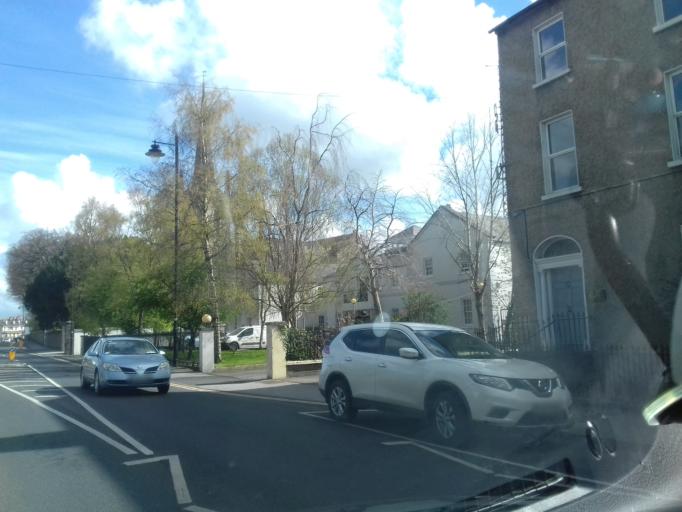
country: IE
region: Ulster
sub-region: An Cabhan
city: Cavan
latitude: 53.9931
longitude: -7.3616
